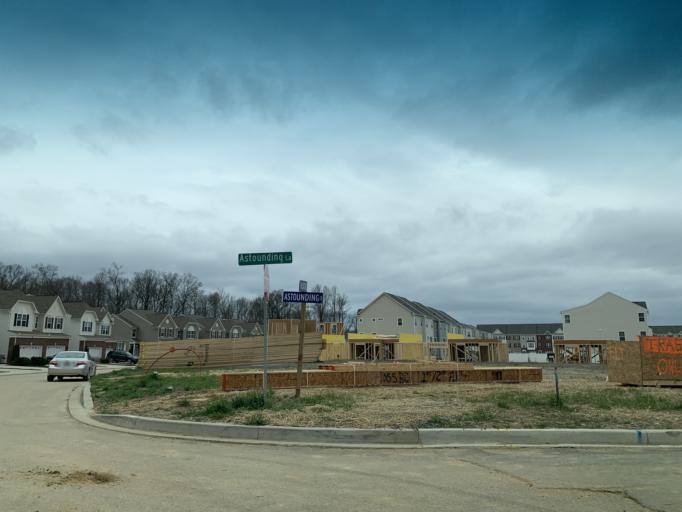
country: US
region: Maryland
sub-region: Harford County
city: Perryman
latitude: 39.4944
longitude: -76.2017
